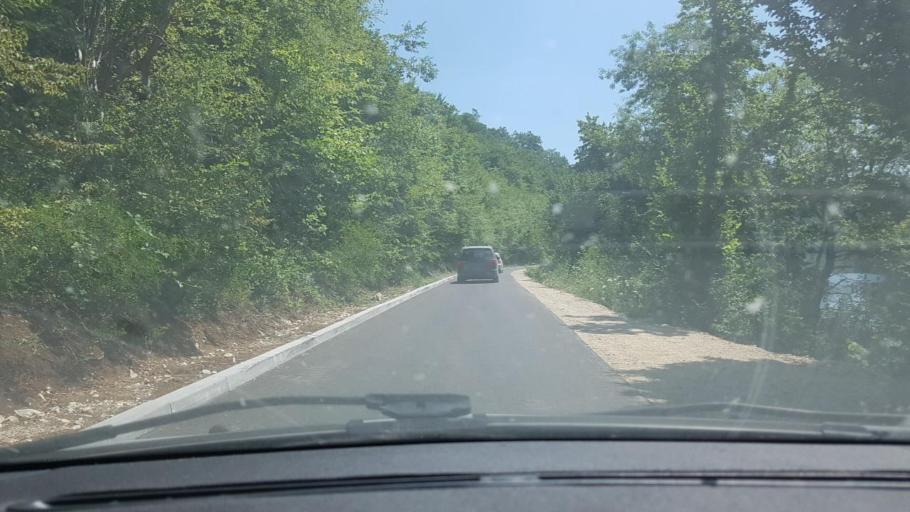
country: BA
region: Federation of Bosnia and Herzegovina
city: Orasac
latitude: 44.6258
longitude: 16.0551
